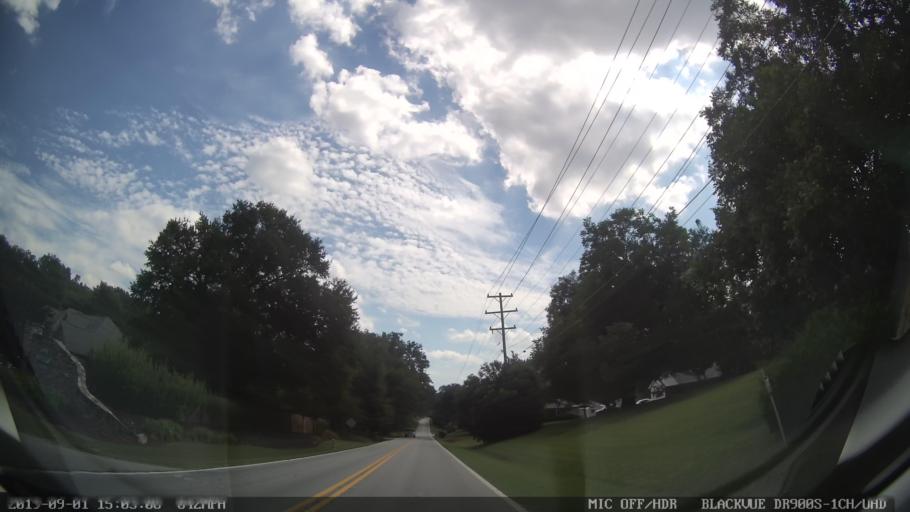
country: US
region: South Carolina
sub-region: Greenville County
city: Greer
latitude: 34.9667
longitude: -82.2014
